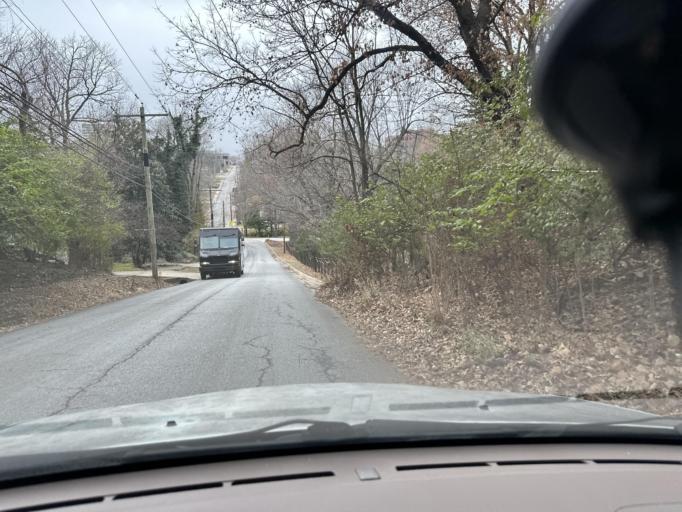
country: US
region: Arkansas
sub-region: Washington County
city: Fayetteville
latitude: 36.0647
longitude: -94.1532
